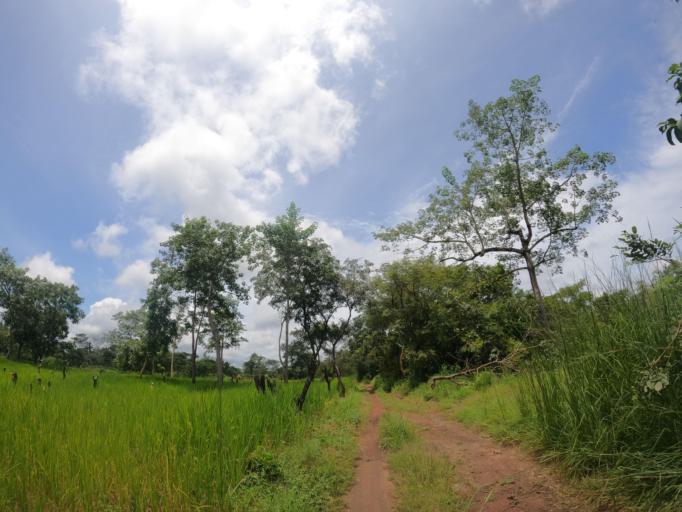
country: SL
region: Northern Province
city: Makeni
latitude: 9.1486
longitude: -12.2513
